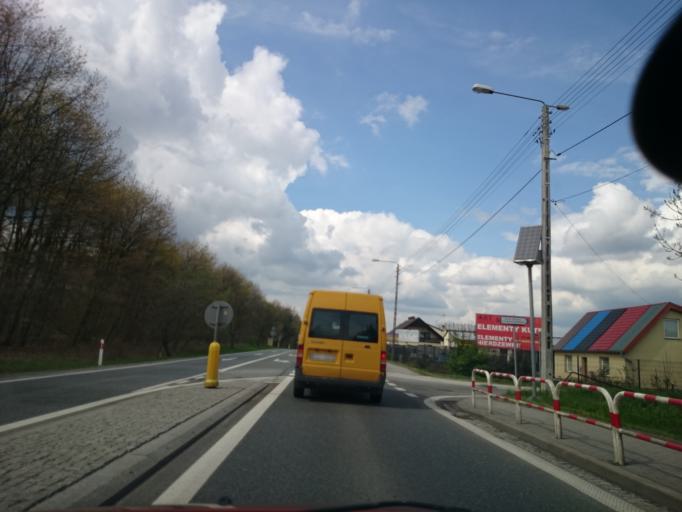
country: PL
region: Opole Voivodeship
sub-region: Powiat opolski
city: Tarnow Opolski
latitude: 50.5999
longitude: 18.0854
